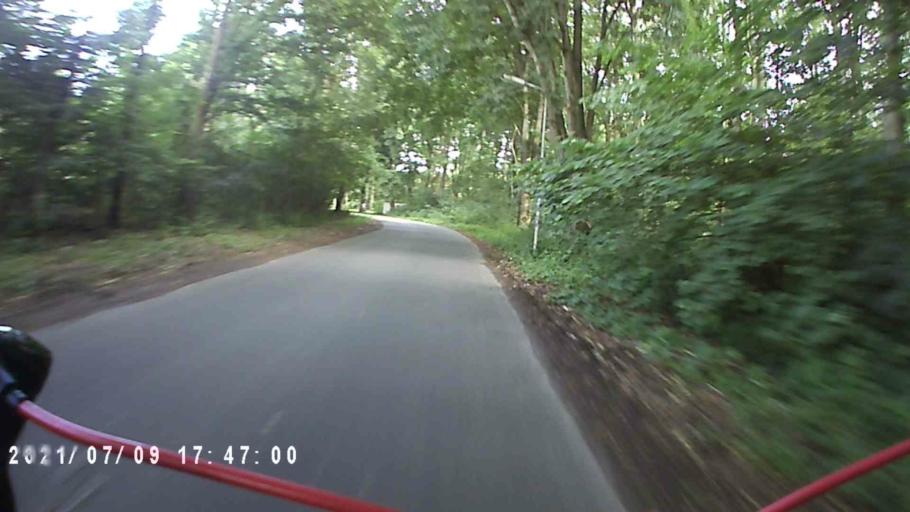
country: NL
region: Groningen
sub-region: Gemeente Vlagtwedde
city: Vlagtwedde
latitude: 53.0829
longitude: 7.0776
